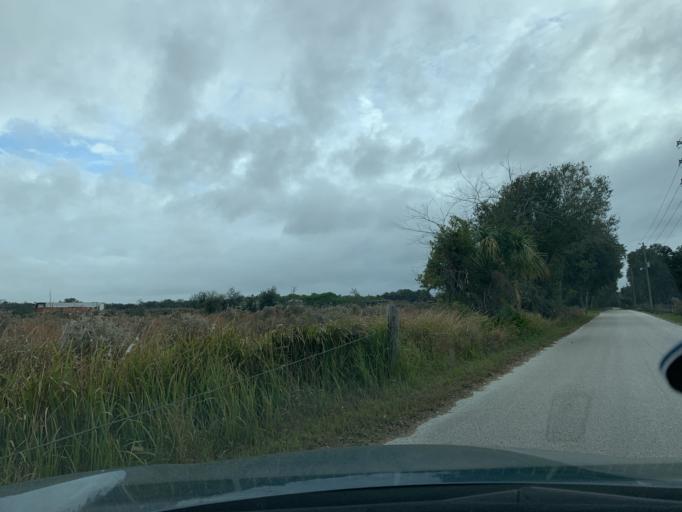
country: US
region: Florida
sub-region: Pasco County
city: San Antonio
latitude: 28.3237
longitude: -82.3579
